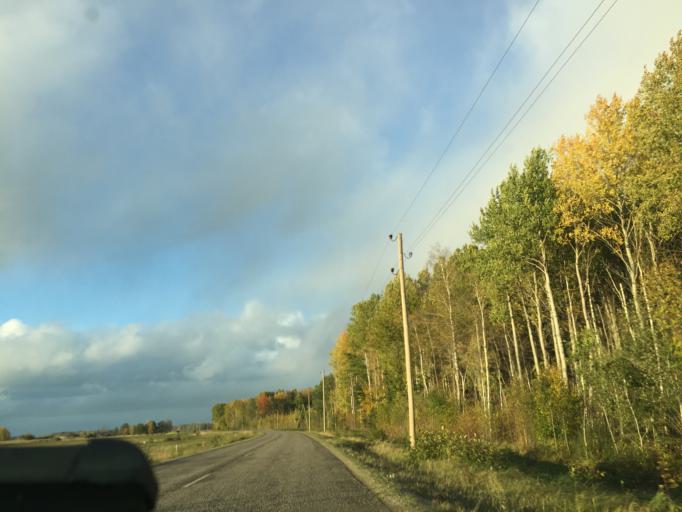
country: LV
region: Broceni
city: Broceni
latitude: 56.8671
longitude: 22.3823
